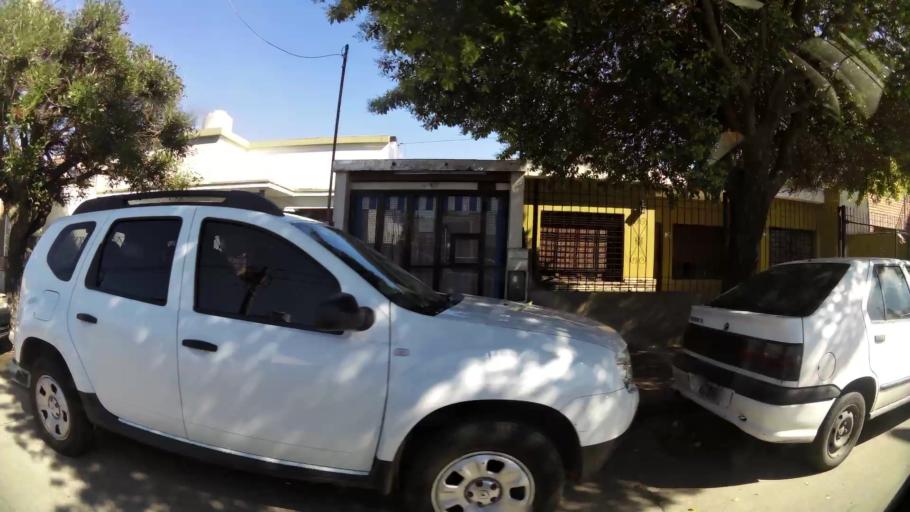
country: AR
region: Cordoba
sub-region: Departamento de Capital
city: Cordoba
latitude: -31.4390
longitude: -64.1586
